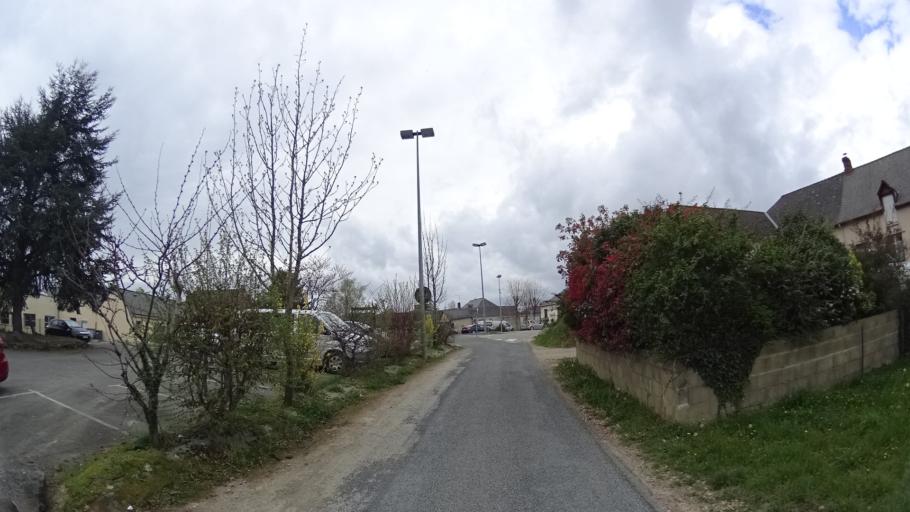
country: FR
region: Brittany
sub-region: Departement d'Ille-et-Vilaine
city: Cintre
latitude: 48.1054
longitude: -1.8692
